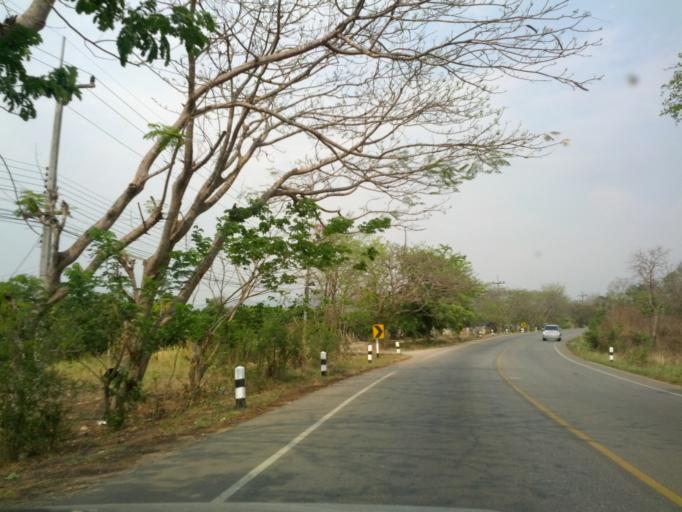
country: TH
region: Chiang Mai
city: Mae Taeng
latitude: 19.1038
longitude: 99.0574
